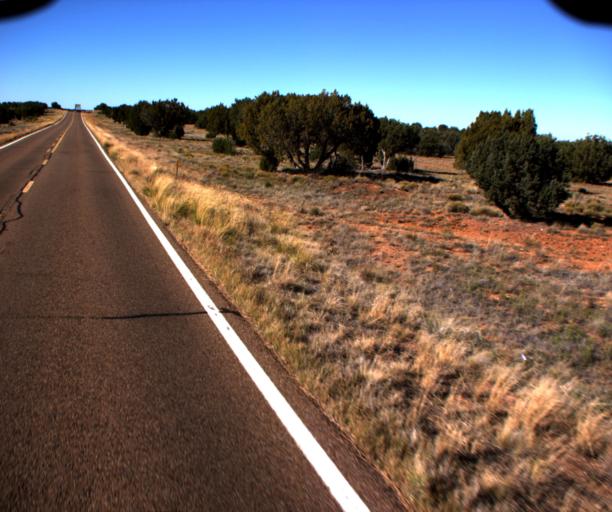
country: US
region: Arizona
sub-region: Navajo County
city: Heber-Overgaard
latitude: 34.5128
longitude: -110.4422
